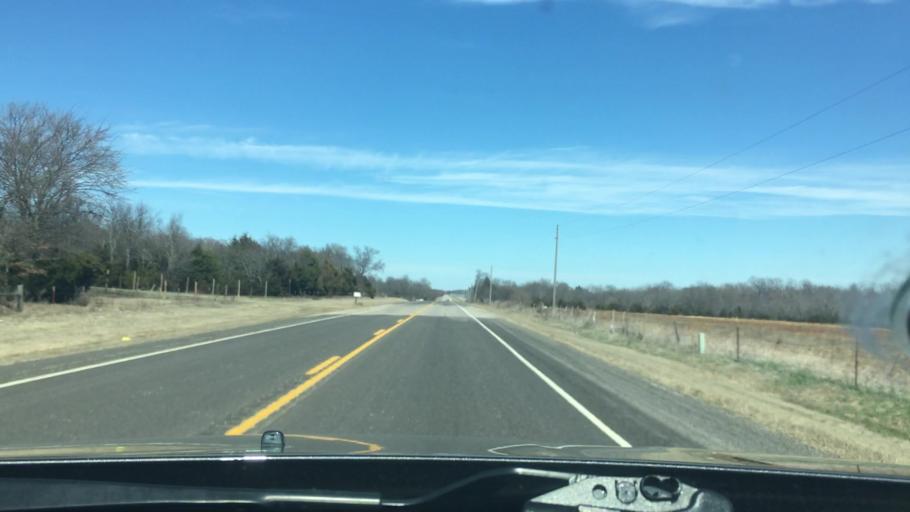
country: US
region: Oklahoma
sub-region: Murray County
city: Sulphur
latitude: 34.3556
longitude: -96.9509
